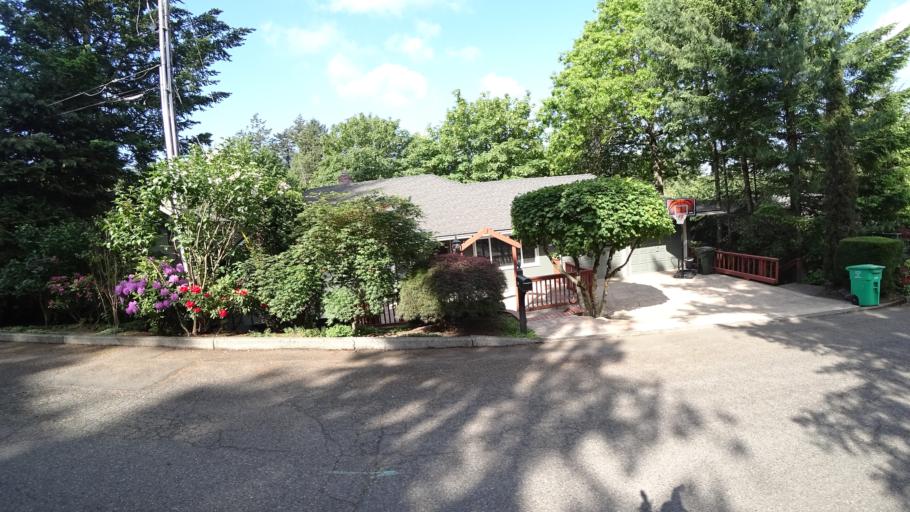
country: US
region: Oregon
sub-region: Washington County
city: West Slope
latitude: 45.5068
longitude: -122.7291
